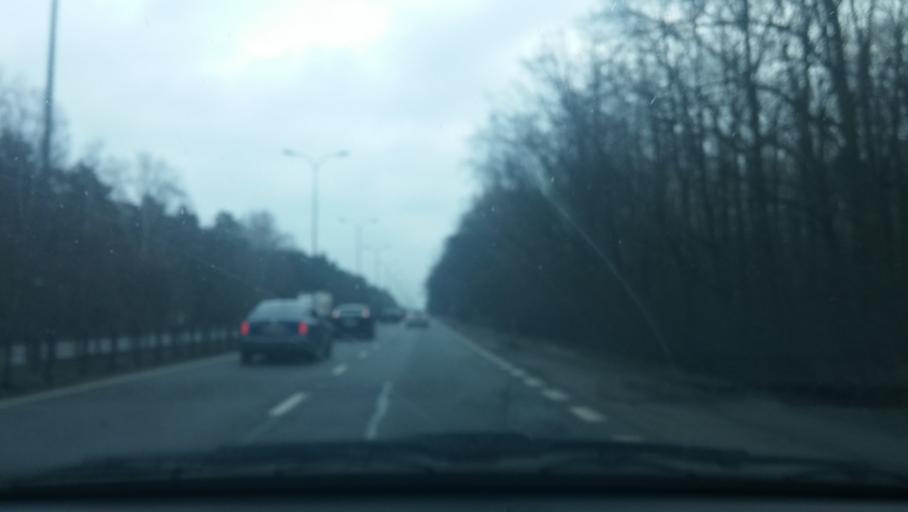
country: PL
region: Masovian Voivodeship
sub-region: Warszawa
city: Wawer
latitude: 52.2253
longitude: 21.1780
